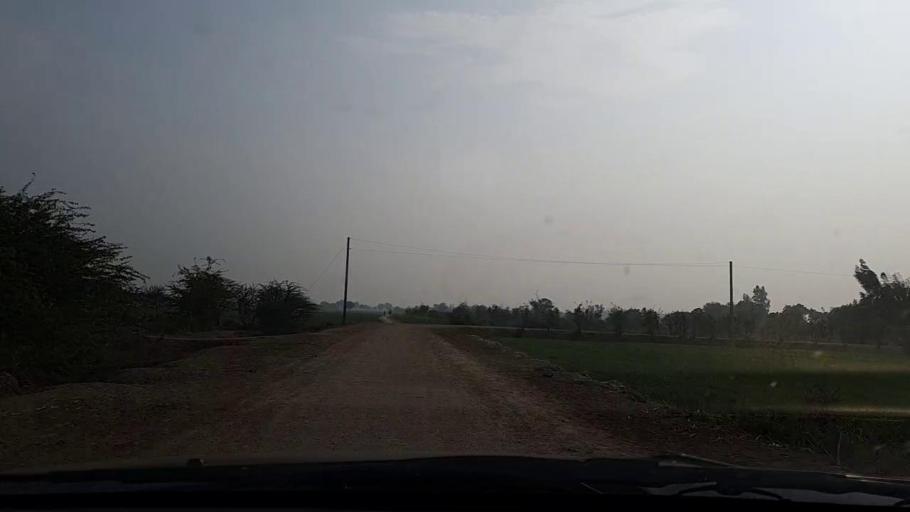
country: PK
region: Sindh
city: Pithoro
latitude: 25.7208
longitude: 69.3901
